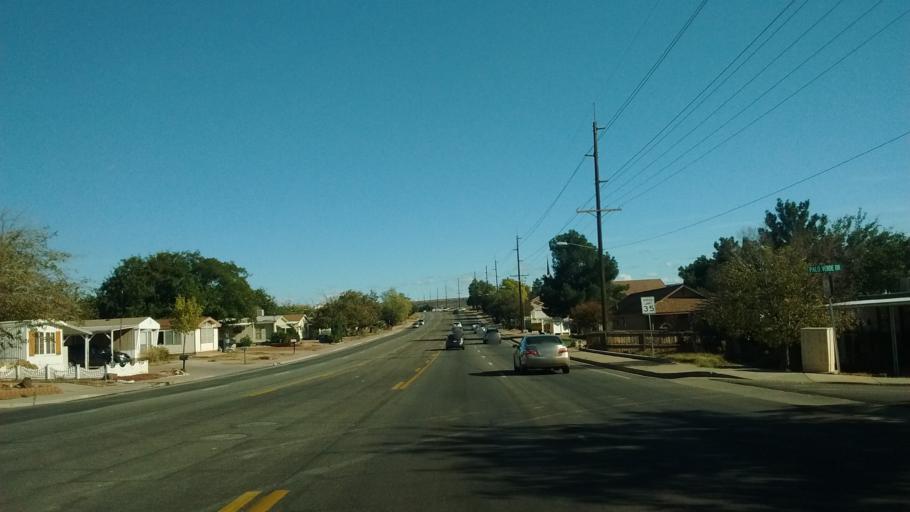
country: US
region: Utah
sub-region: Washington County
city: Washington
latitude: 37.1302
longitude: -113.5029
